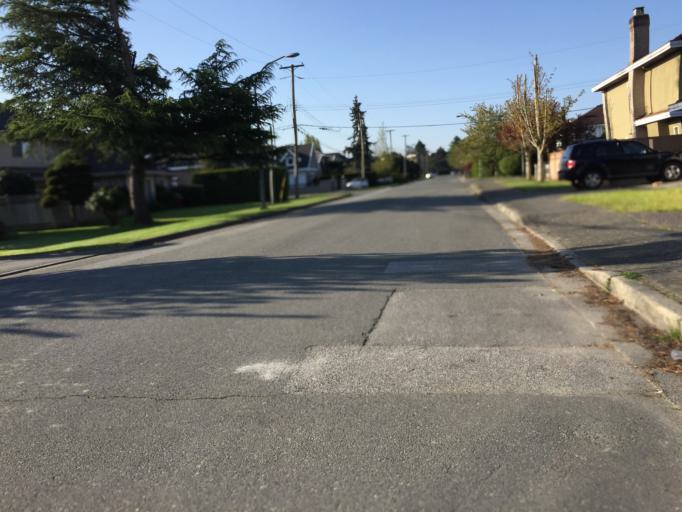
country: CA
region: British Columbia
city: Richmond
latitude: 49.1507
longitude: -123.1398
